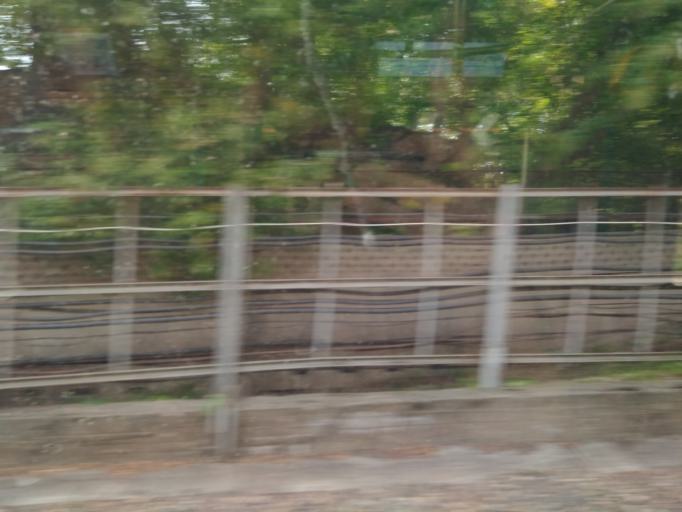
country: RU
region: Moskovskaya
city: Presnenskiy
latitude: 55.7435
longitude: 37.5226
